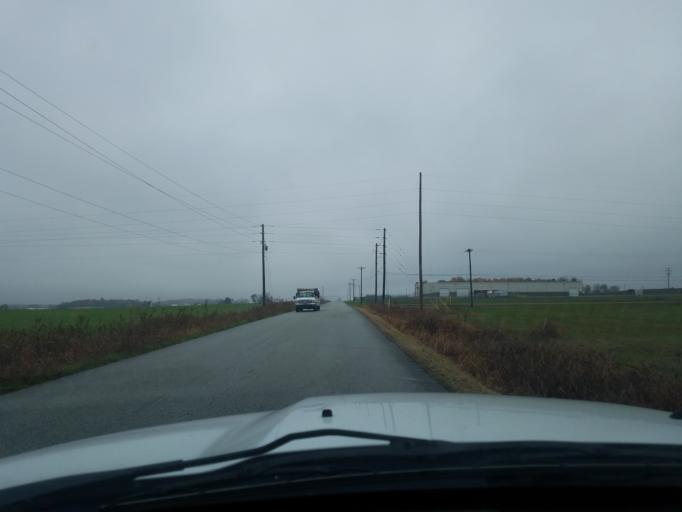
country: US
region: Kentucky
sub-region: Taylor County
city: Campbellsville
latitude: 37.3417
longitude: -85.3285
